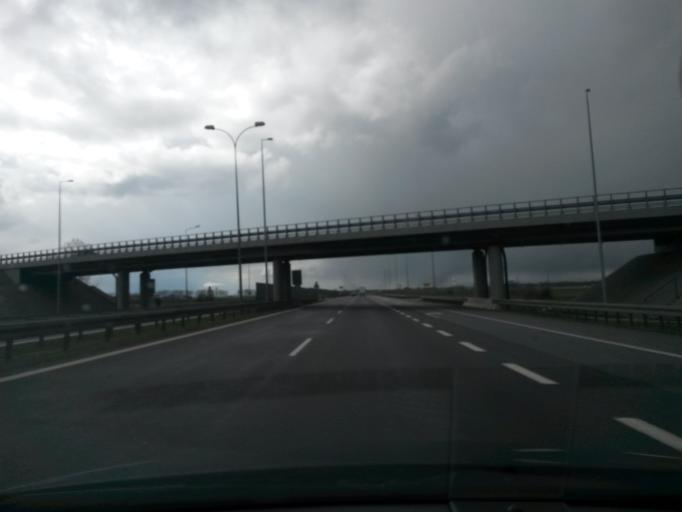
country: PL
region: Greater Poland Voivodeship
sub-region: Powiat poznanski
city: Kleszczewo
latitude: 52.3124
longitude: 17.1456
